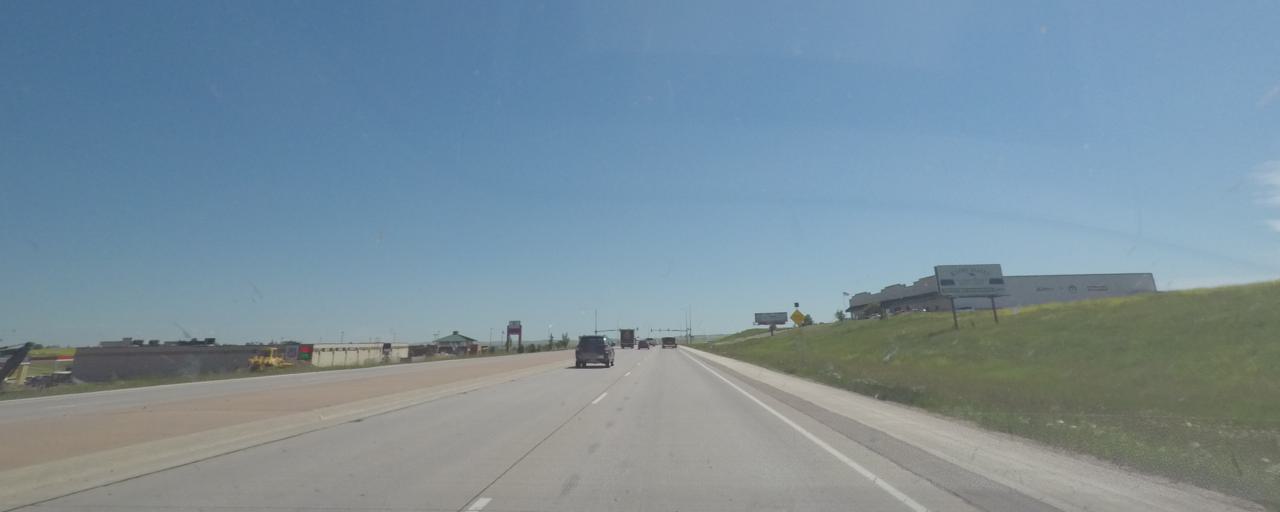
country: US
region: South Dakota
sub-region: Pennington County
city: Rapid Valley
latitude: 44.0786
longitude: -103.1515
